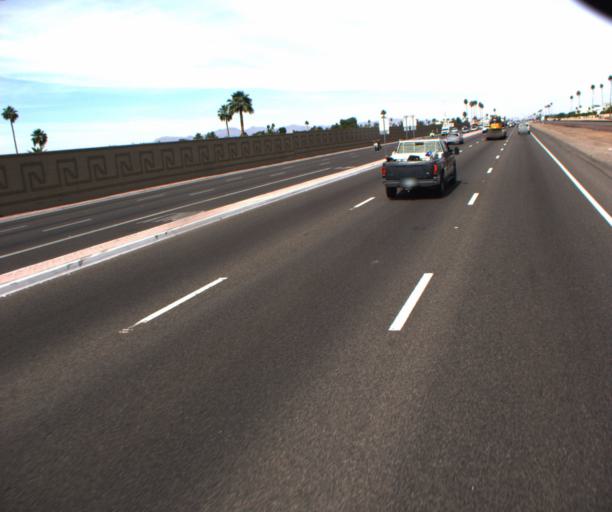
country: US
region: Arizona
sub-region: Maricopa County
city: Sun City
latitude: 33.5979
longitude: -112.2730
